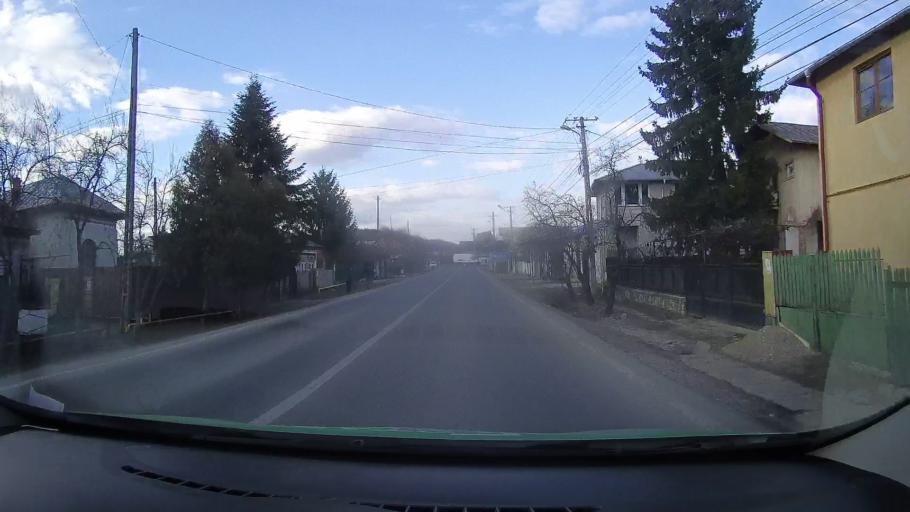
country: RO
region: Dambovita
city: Razvad
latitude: 44.9345
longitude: 25.5333
